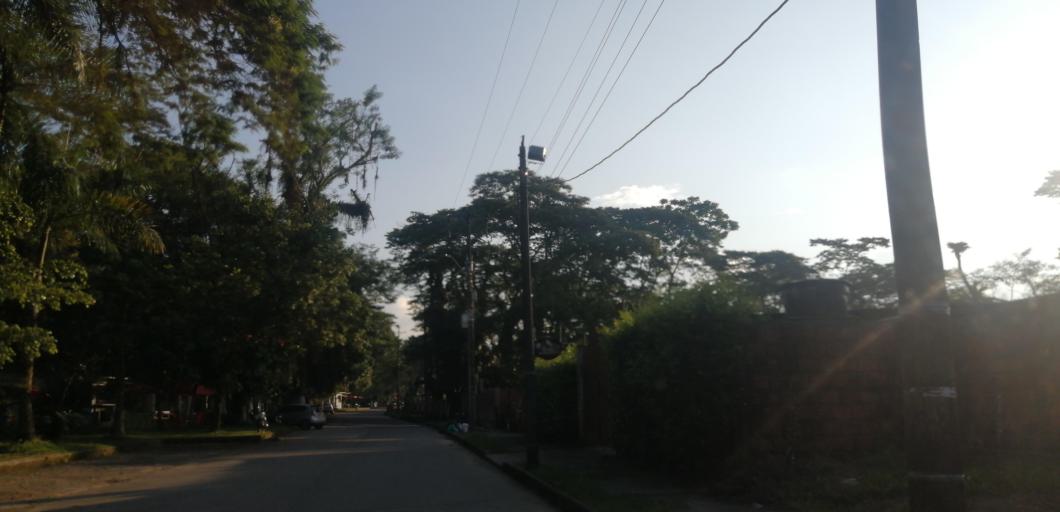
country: CO
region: Meta
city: Acacias
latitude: 3.9769
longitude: -73.7604
